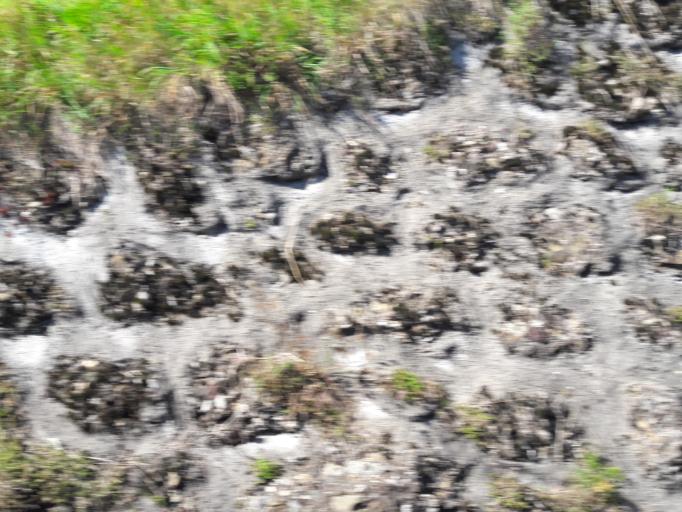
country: CH
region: Schwyz
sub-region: Bezirk Schwyz
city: Sattel
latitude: 47.0826
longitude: 8.6368
